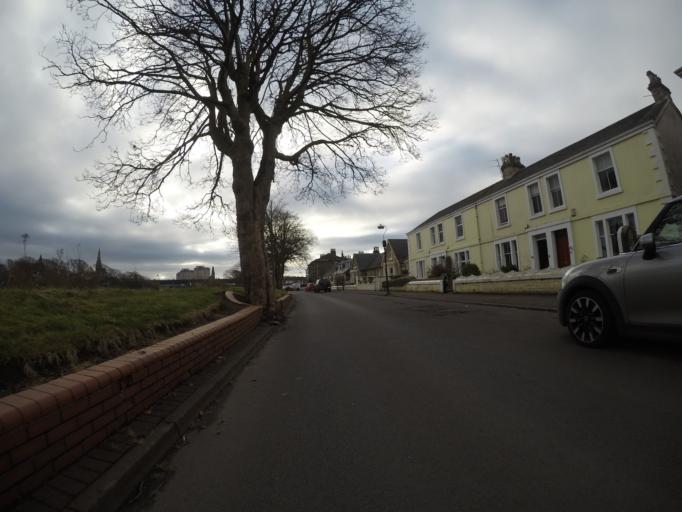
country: GB
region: Scotland
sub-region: North Ayrshire
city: Irvine
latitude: 55.6160
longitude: -4.6746
